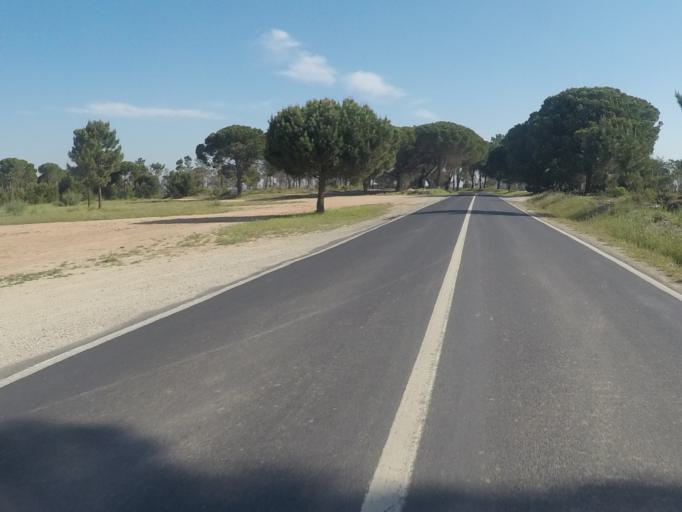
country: PT
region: Setubal
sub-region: Sesimbra
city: Sesimbra
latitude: 38.5160
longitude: -9.1441
